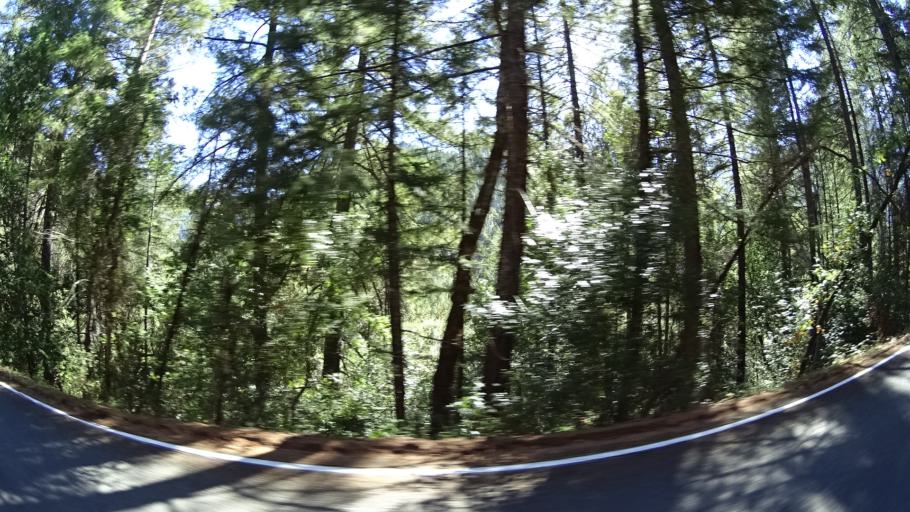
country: US
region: California
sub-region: Siskiyou County
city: Happy Camp
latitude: 41.3777
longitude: -123.4420
